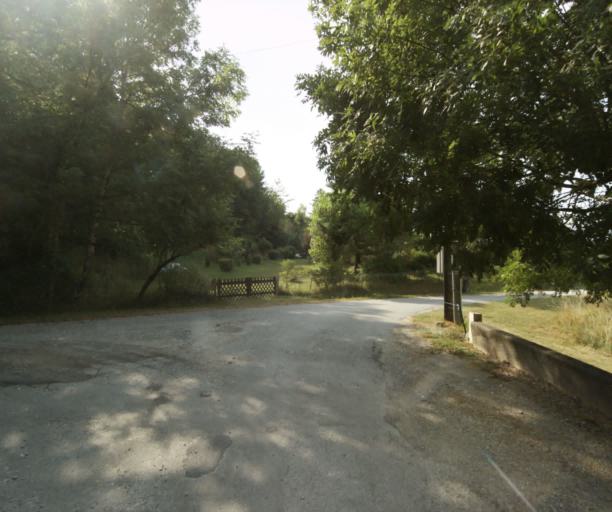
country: FR
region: Midi-Pyrenees
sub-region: Departement de la Haute-Garonne
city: Revel
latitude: 43.4401
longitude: 2.0349
